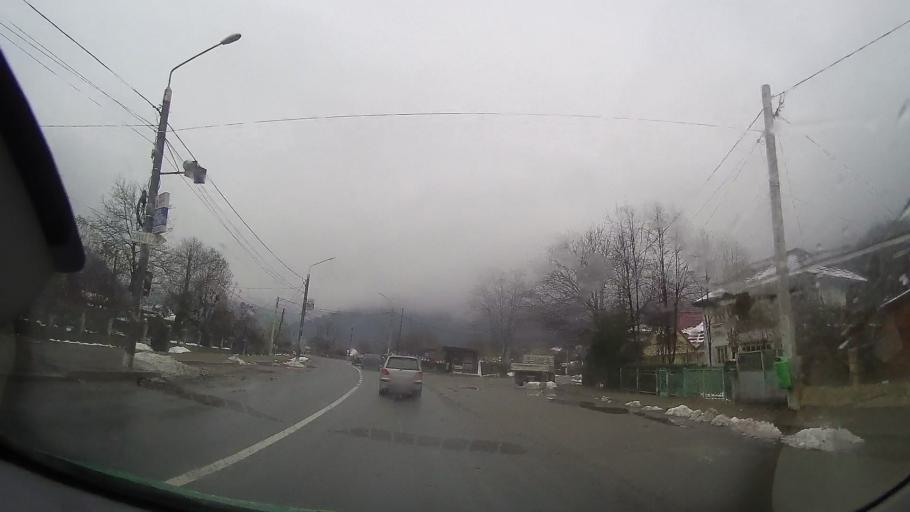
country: RO
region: Neamt
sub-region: Comuna Bicaz
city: Dodeni
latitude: 46.9055
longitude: 26.1085
